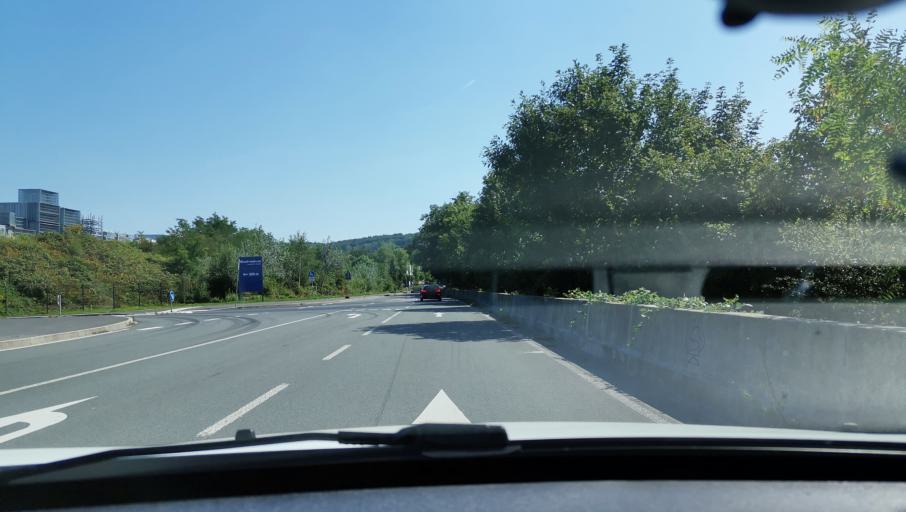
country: DE
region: North Rhine-Westphalia
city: Wetter (Ruhr)
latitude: 51.3819
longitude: 7.4094
